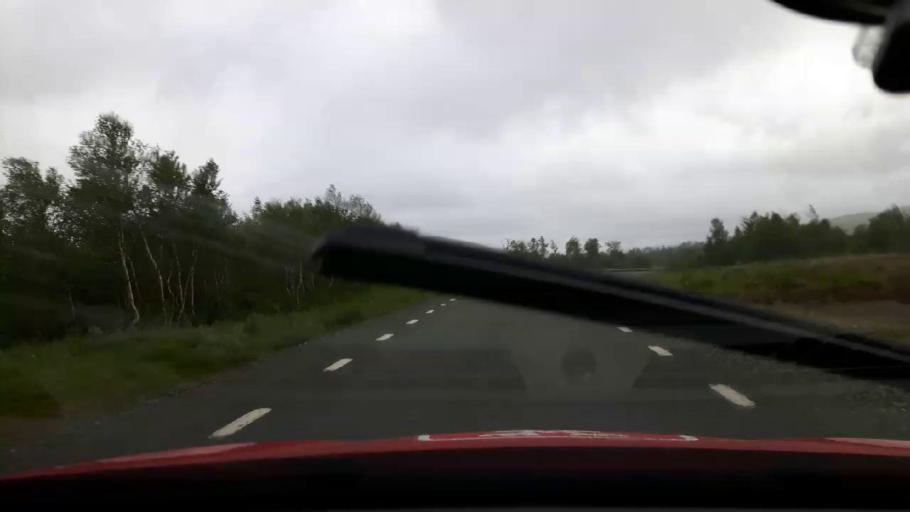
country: NO
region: Nord-Trondelag
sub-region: Meraker
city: Meraker
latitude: 63.1753
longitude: 12.3743
